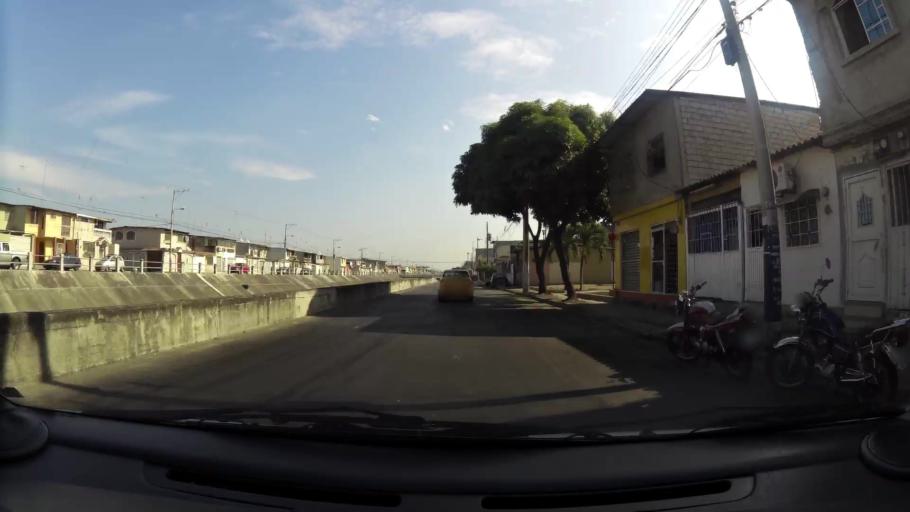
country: EC
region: Guayas
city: Eloy Alfaro
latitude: -2.0934
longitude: -79.9175
